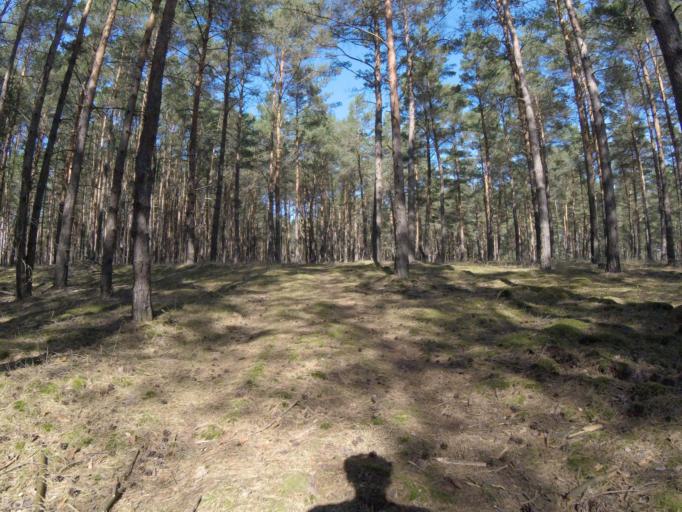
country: DE
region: Brandenburg
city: Bestensee
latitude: 52.2745
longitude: 13.6746
